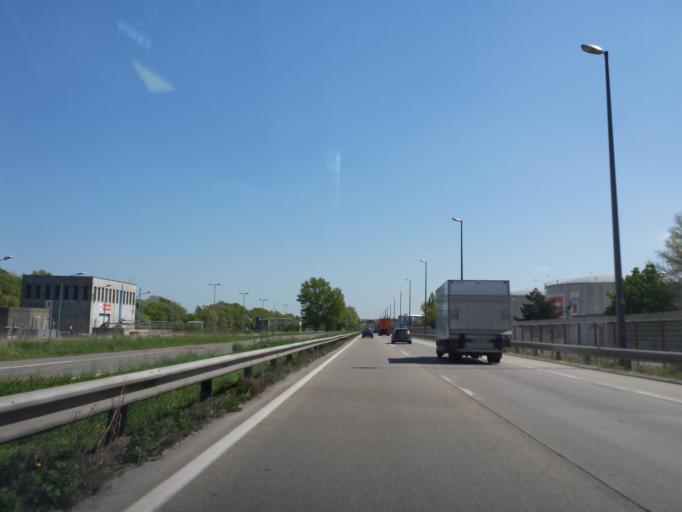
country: AT
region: Lower Austria
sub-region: Politischer Bezirk Wien-Umgebung
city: Schwechat
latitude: 48.1849
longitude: 16.4347
